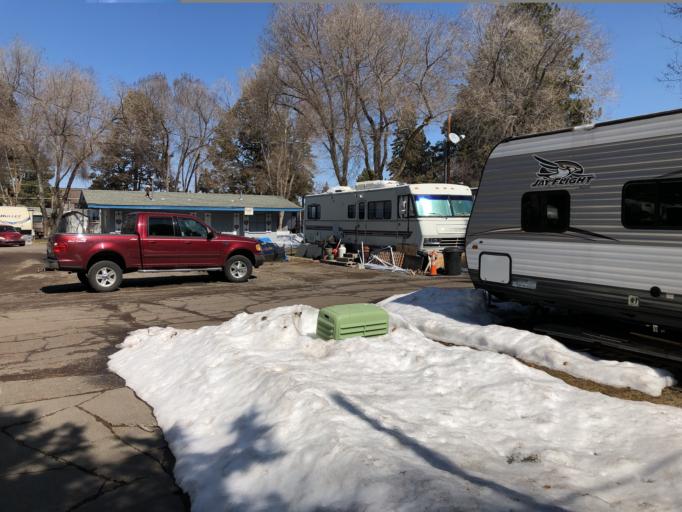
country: US
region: Oregon
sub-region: Deschutes County
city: Bend
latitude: 44.0314
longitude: -121.3118
